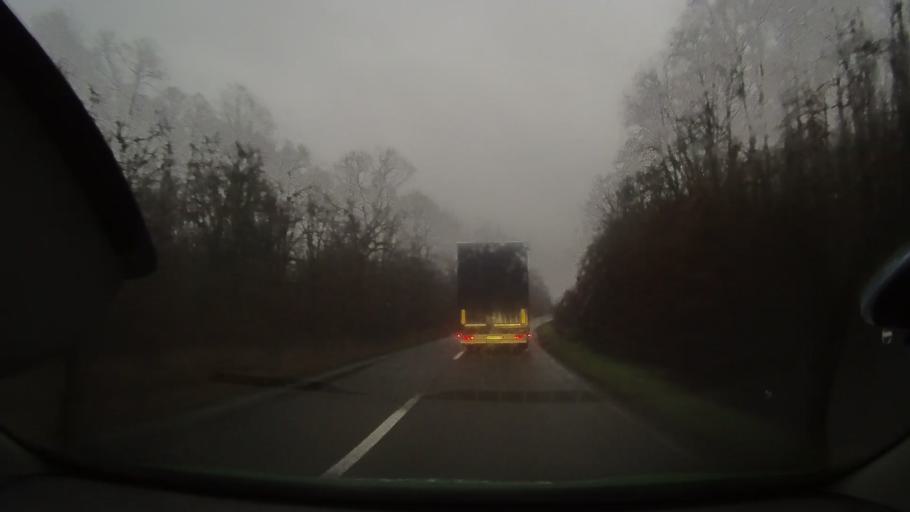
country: RO
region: Arad
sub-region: Comuna Beliu
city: Beliu
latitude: 46.5044
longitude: 21.9722
